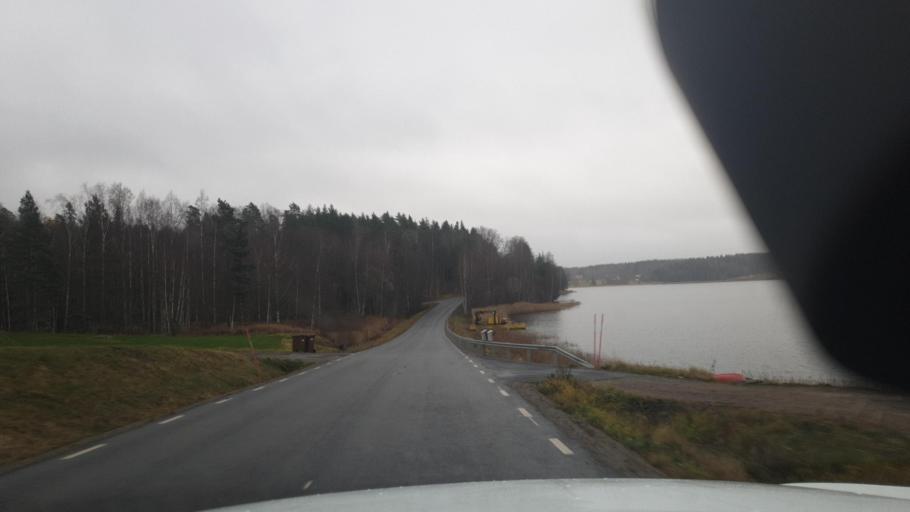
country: SE
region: Vaermland
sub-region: Arvika Kommun
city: Arvika
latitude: 59.6637
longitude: 12.6907
